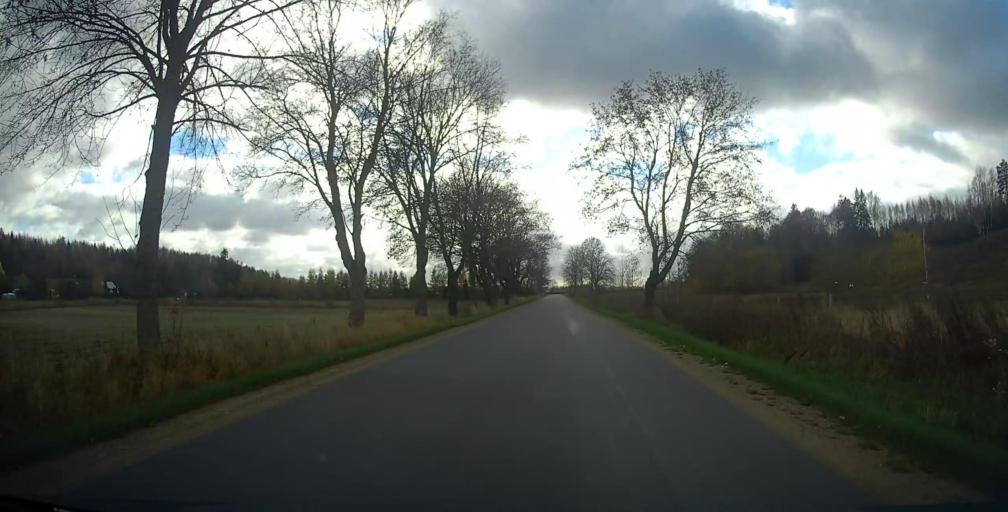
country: PL
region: Podlasie
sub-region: Suwalki
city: Suwalki
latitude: 54.3016
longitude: 22.8791
